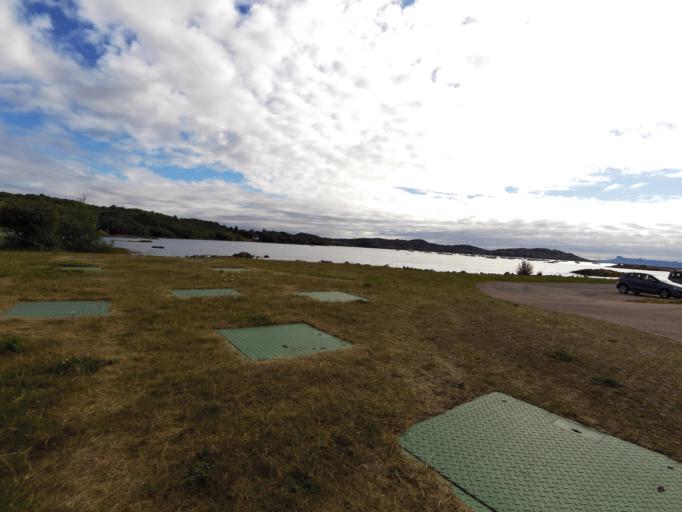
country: GB
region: Scotland
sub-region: Argyll and Bute
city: Isle Of Mull
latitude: 56.9093
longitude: -5.8451
